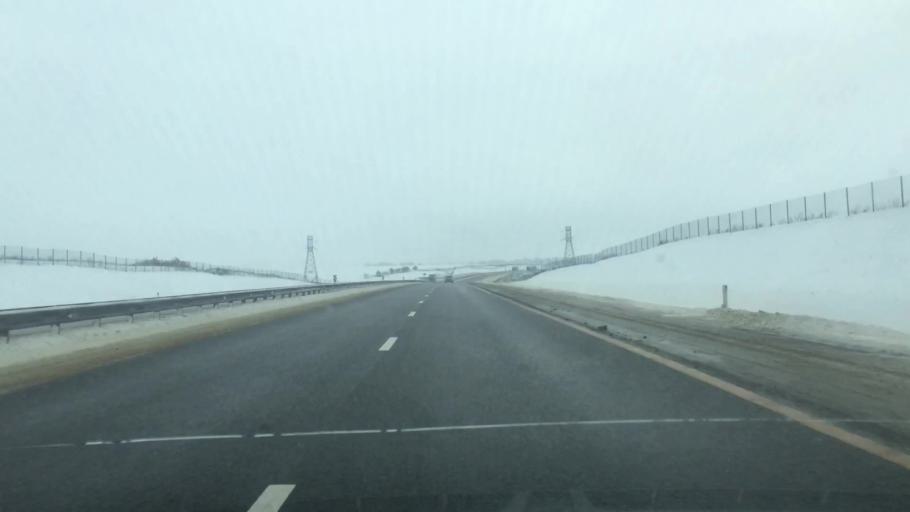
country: RU
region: Tula
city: Yefremov
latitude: 53.1463
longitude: 38.2489
